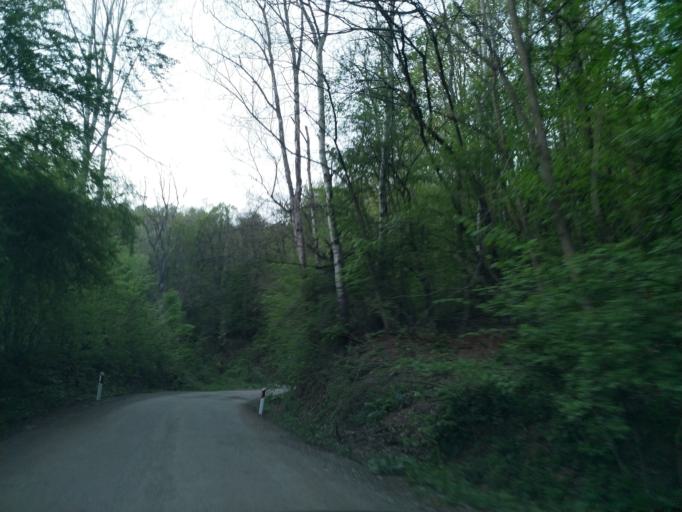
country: RS
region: Central Serbia
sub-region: Pomoravski Okrug
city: Despotovac
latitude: 43.9614
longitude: 21.5632
